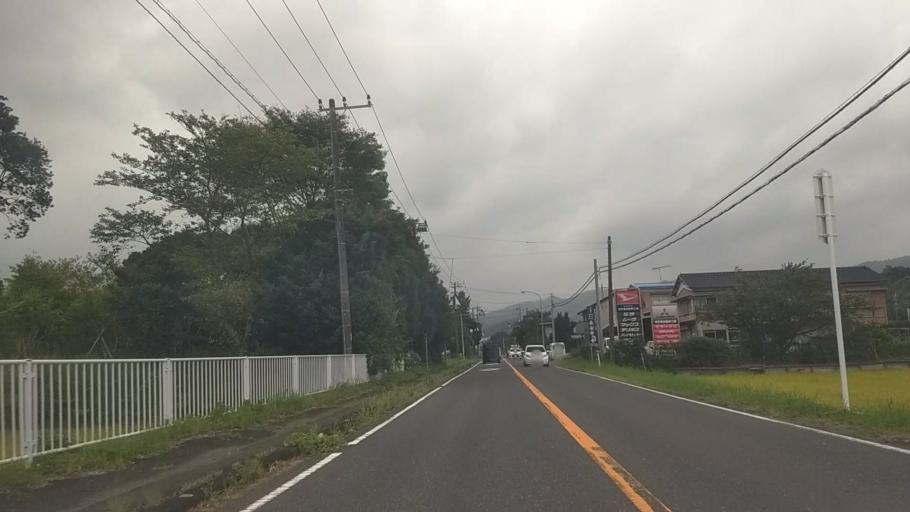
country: JP
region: Chiba
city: Kawaguchi
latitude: 35.1340
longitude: 140.0052
